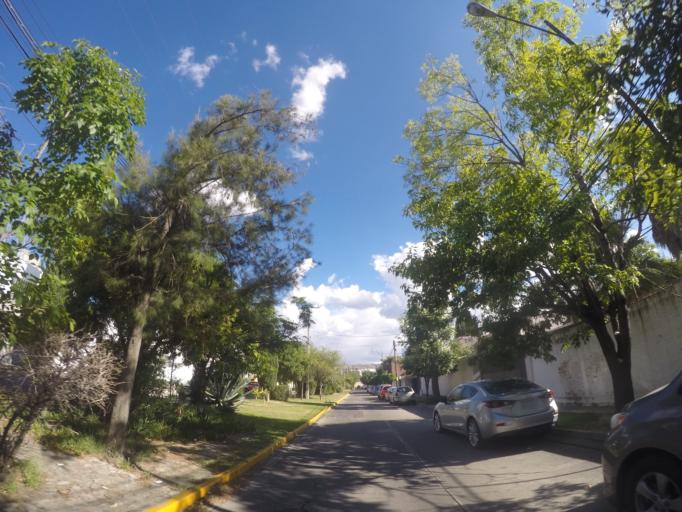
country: MX
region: San Luis Potosi
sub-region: San Luis Potosi
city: San Luis Potosi
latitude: 22.1425
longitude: -101.0209
